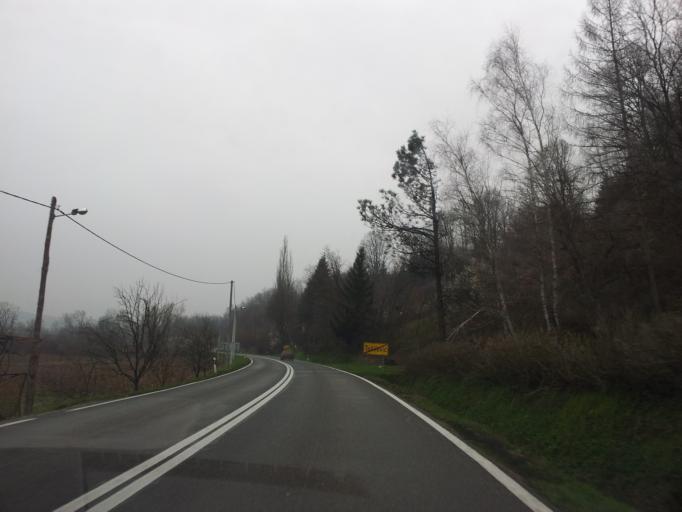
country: HR
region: Karlovacka
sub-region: Grad Karlovac
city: Karlovac
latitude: 45.4062
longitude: 15.6135
